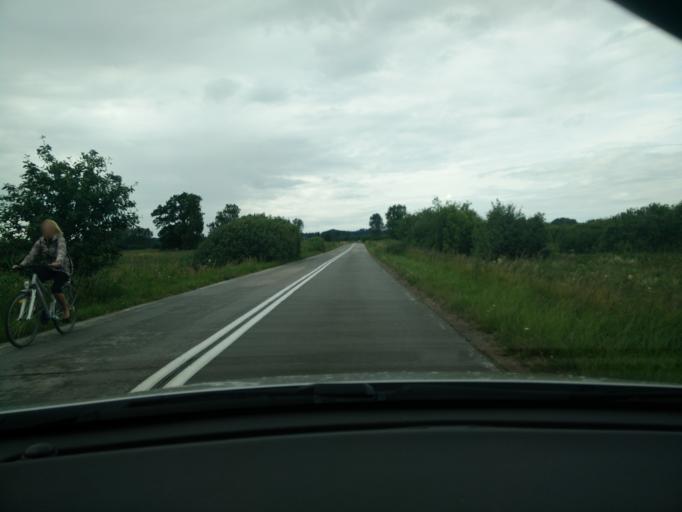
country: PL
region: Pomeranian Voivodeship
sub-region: Powiat pucki
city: Mrzezino
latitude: 54.6230
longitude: 18.4393
